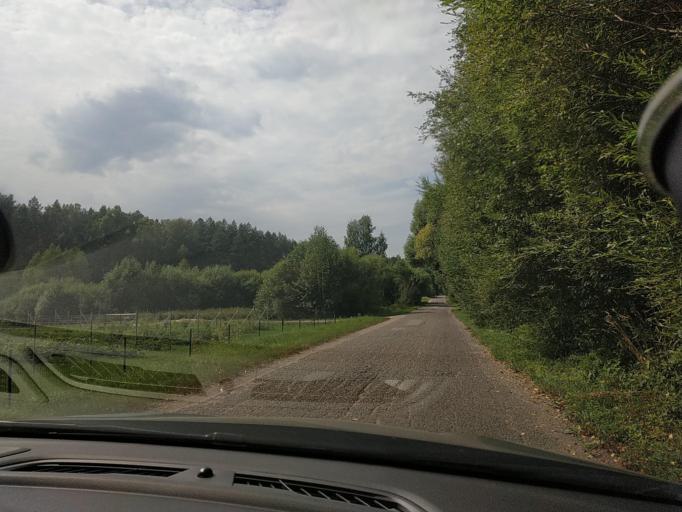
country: LT
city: Nemencine
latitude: 54.8532
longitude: 25.4461
